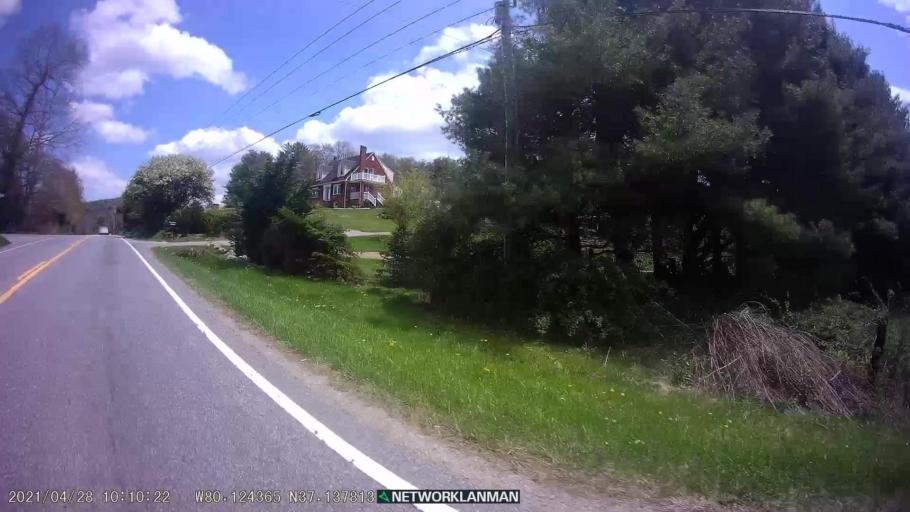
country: US
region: Virginia
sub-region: Montgomery County
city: Shawsville
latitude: 37.1380
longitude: -80.1240
